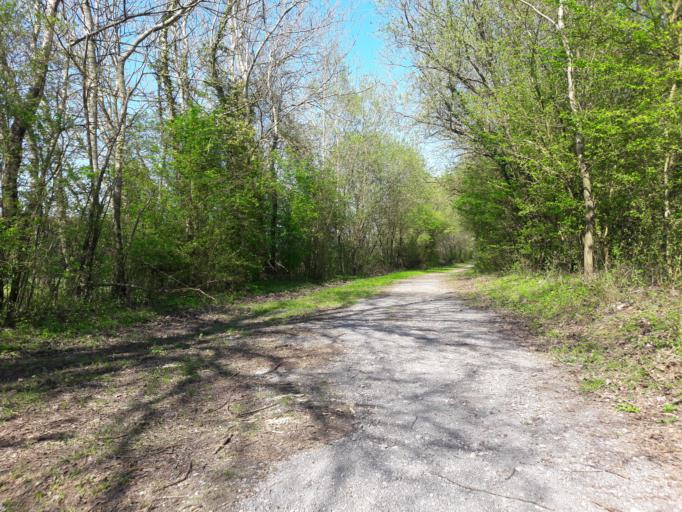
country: FR
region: Nord-Pas-de-Calais
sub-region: Departement du Nord
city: Sains-du-Nord
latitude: 50.1688
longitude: 4.0759
